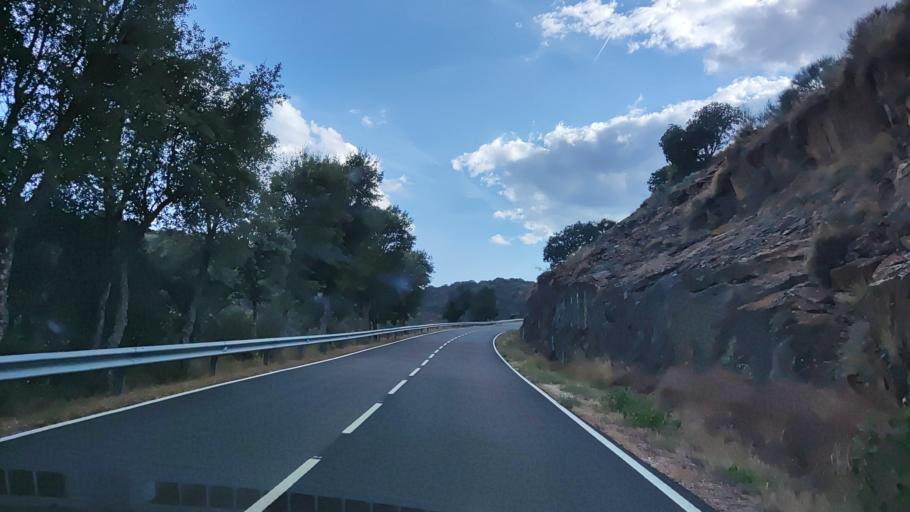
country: ES
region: Castille and Leon
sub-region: Provincia de Salamanca
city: Pastores
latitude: 40.4947
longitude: -6.4980
